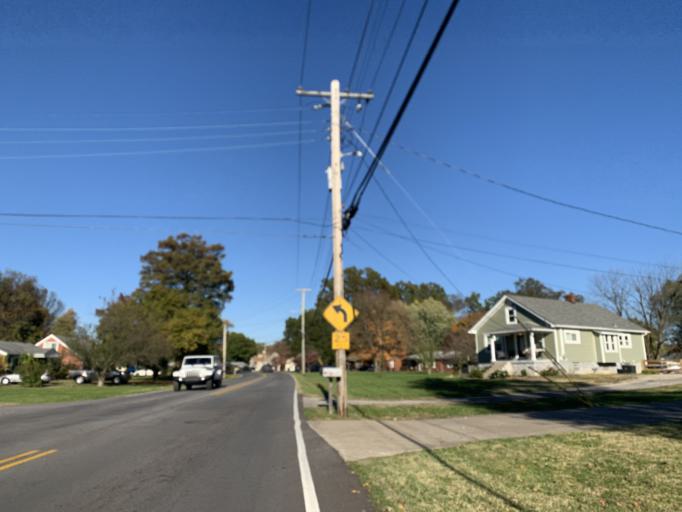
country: US
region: Kentucky
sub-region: Jefferson County
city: Pleasure Ridge Park
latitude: 38.1588
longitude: -85.8467
